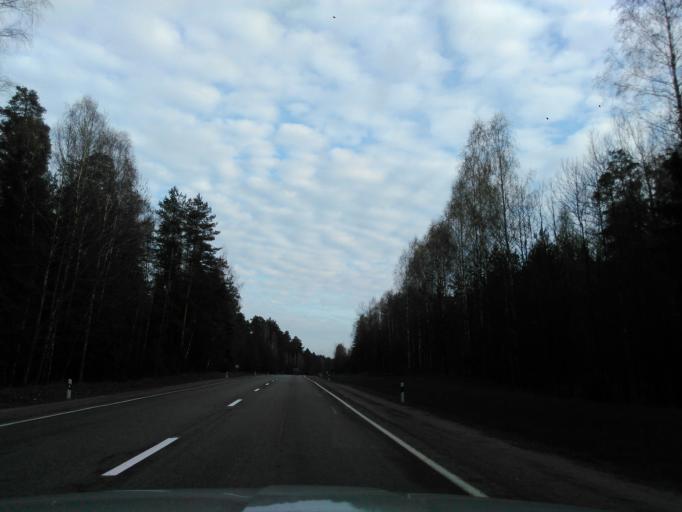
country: BY
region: Minsk
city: Plyeshchanitsy
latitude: 54.3787
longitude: 27.8780
